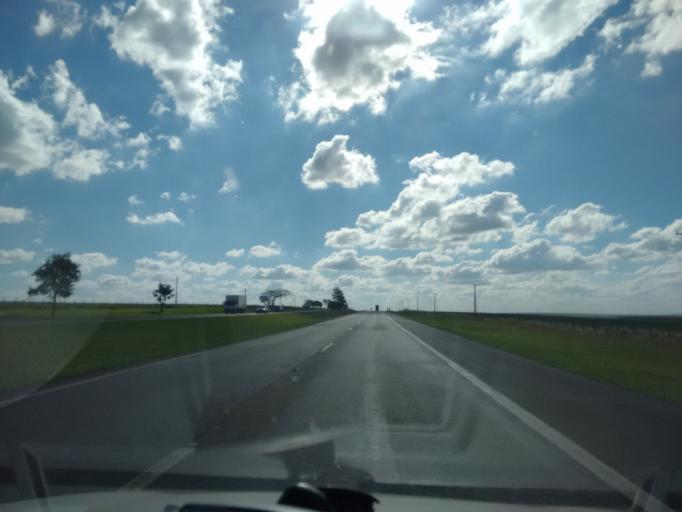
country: BR
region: Sao Paulo
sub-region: Ibate
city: Ibate
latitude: -21.9037
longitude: -48.0576
